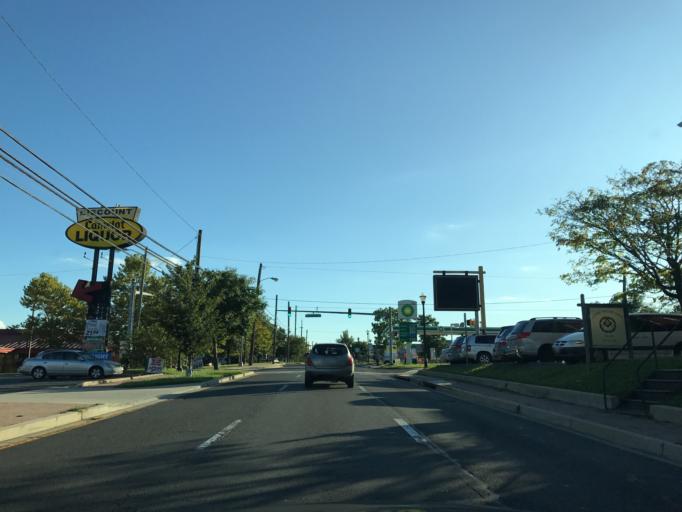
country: US
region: Maryland
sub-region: Prince George's County
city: Laurel
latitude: 39.1026
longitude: -76.8452
